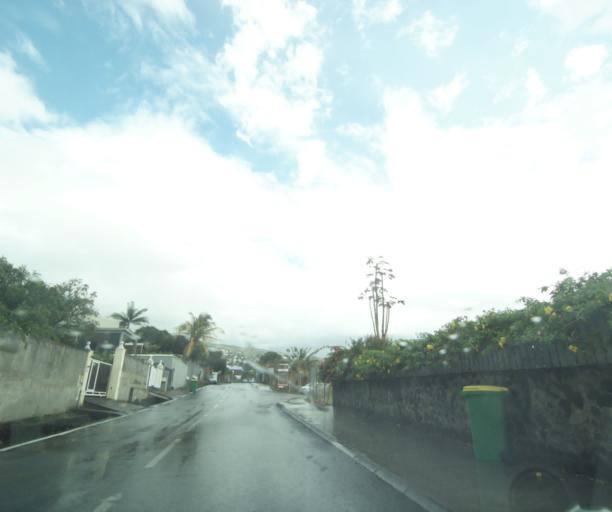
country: RE
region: Reunion
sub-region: Reunion
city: La Possession
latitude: -20.9798
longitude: 55.3284
